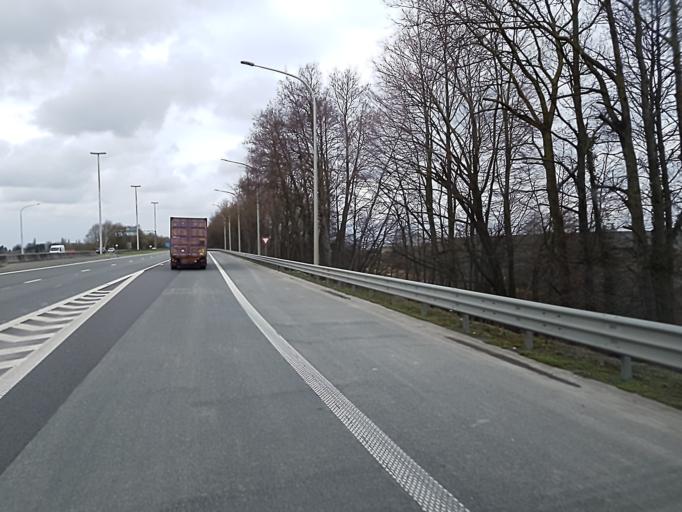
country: FR
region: Nord-Pas-de-Calais
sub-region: Departement du Nord
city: Camphin-en-Pevele
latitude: 50.6179
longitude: 3.3214
